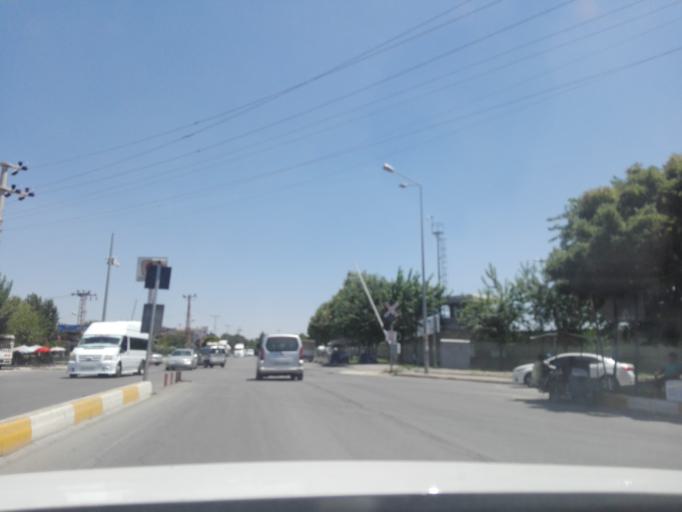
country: TR
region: Batman
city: Batman
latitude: 37.8854
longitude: 41.1382
